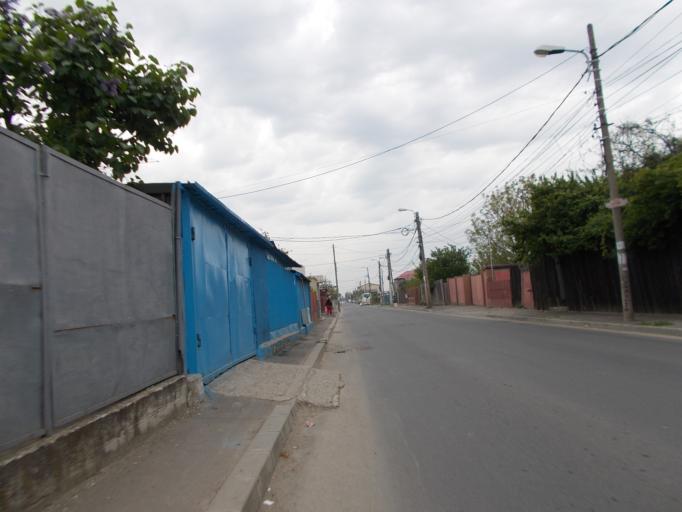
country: RO
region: Ilfov
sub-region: Comuna Jilava
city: Jilava
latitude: 44.3699
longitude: 26.1037
